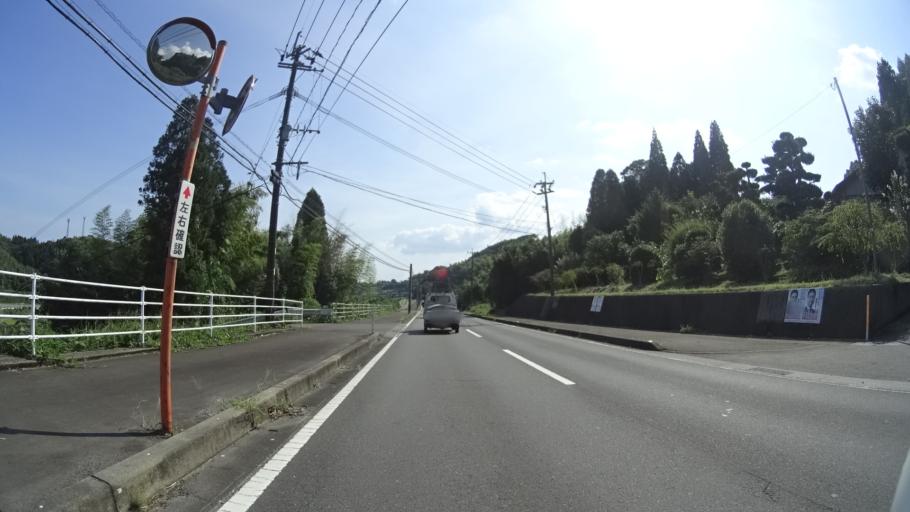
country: JP
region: Kagoshima
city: Kagoshima-shi
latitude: 31.6623
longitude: 130.5519
